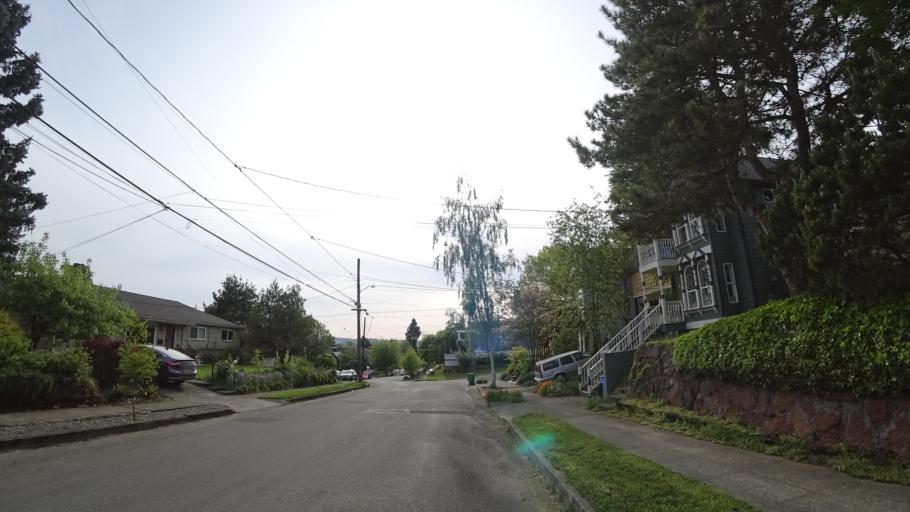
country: US
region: Oregon
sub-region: Clackamas County
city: Milwaukie
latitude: 45.4719
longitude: -122.6205
